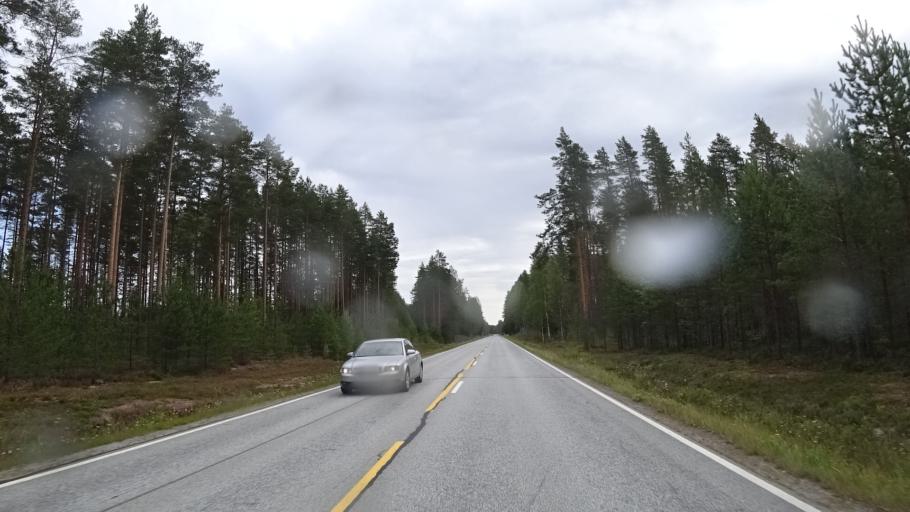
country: FI
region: North Karelia
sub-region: Keski-Karjala
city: Raeaekkylae
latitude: 62.1105
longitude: 29.7302
